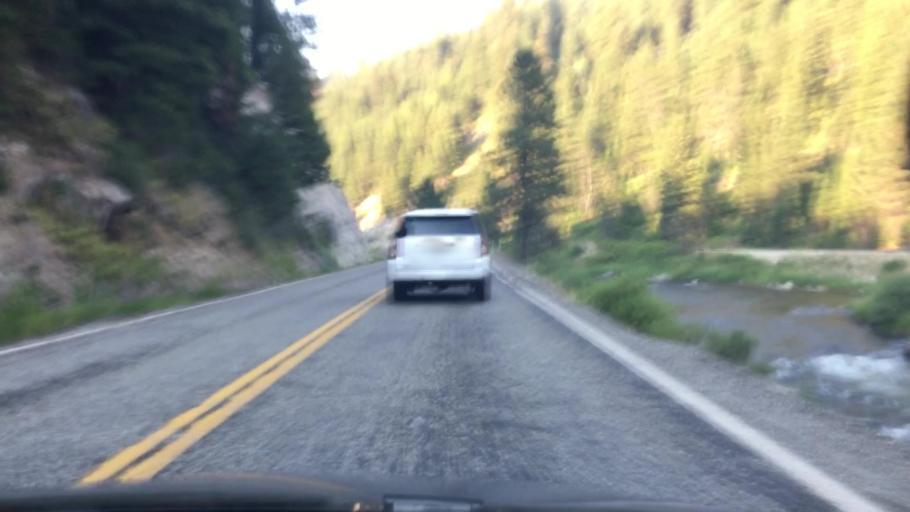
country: US
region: Idaho
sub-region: Valley County
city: Cascade
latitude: 44.3185
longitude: -116.0626
